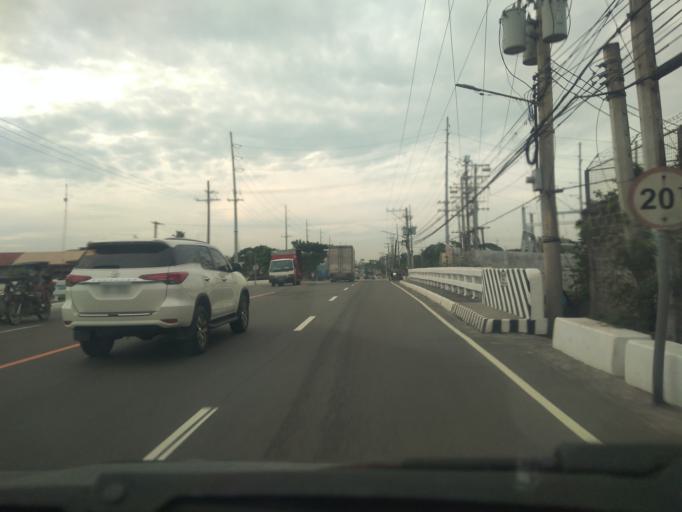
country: PH
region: Central Luzon
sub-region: Province of Pampanga
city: San Fernando
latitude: 15.0278
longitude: 120.6972
